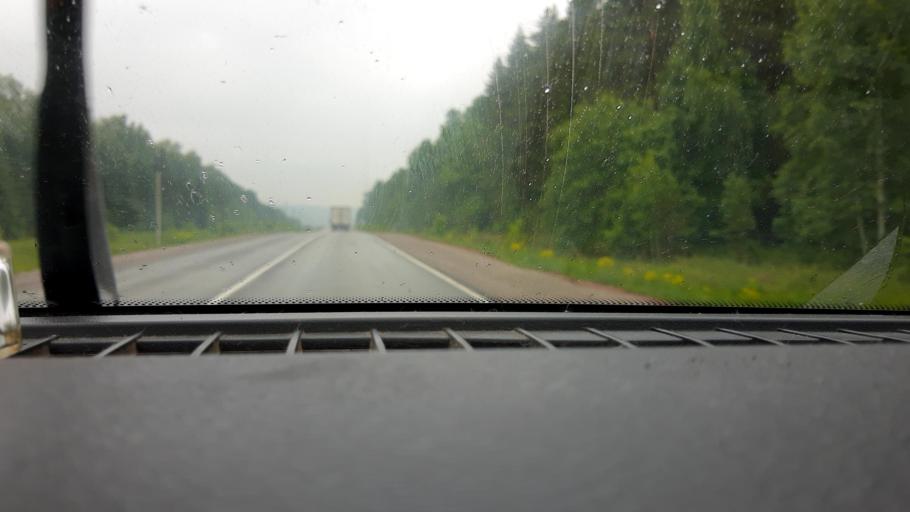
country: RU
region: Bashkortostan
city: Belebey
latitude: 54.2186
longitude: 54.0756
